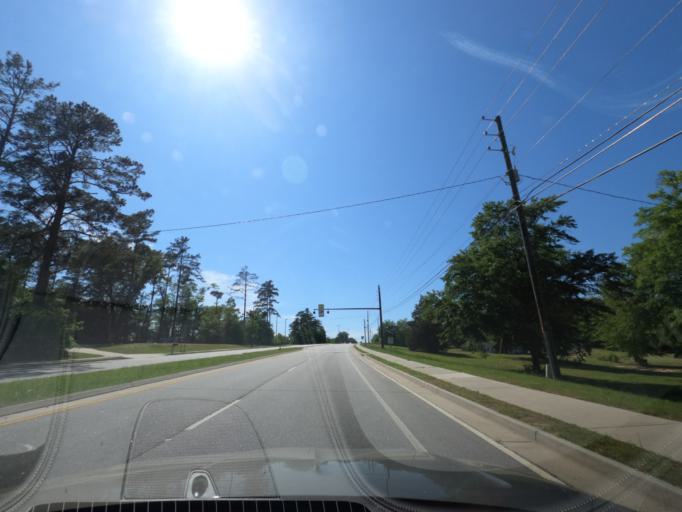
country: US
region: Georgia
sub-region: Columbia County
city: Martinez
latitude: 33.4707
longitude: -82.1075
